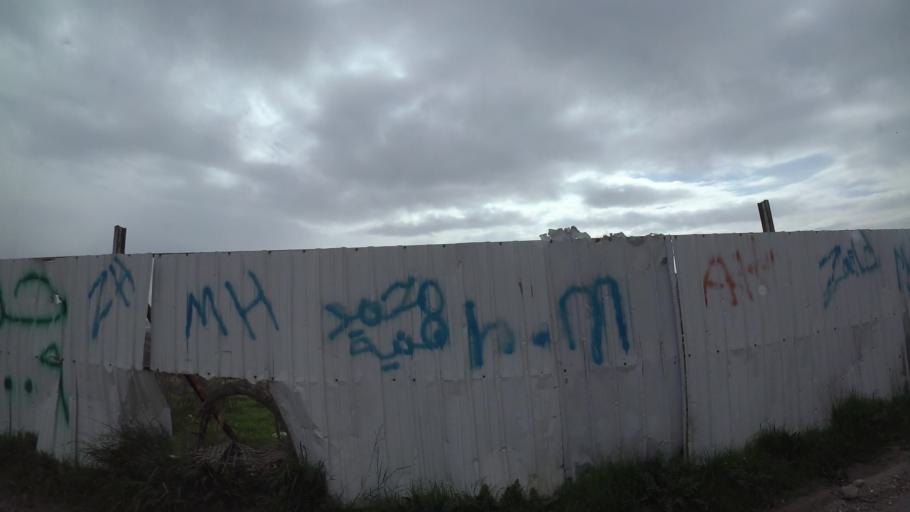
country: JO
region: Amman
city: Umm as Summaq
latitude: 31.8965
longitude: 35.8461
